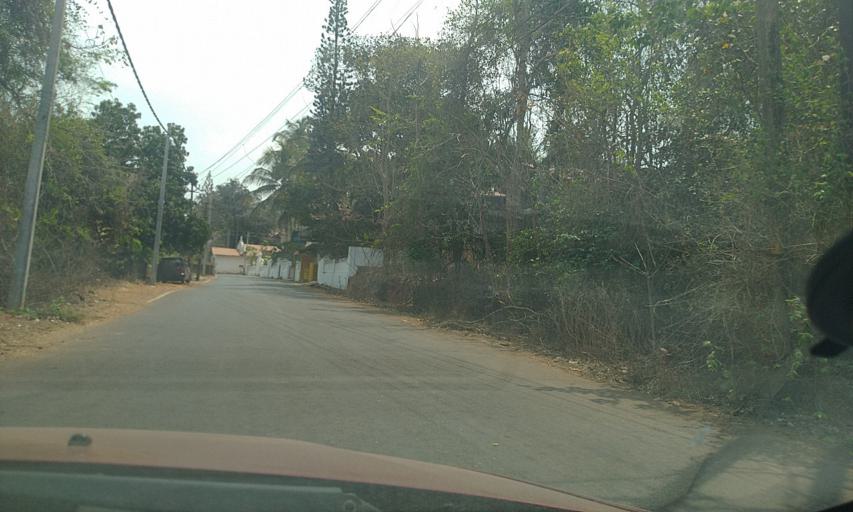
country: IN
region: Goa
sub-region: North Goa
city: Solim
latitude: 15.5916
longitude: 73.7729
